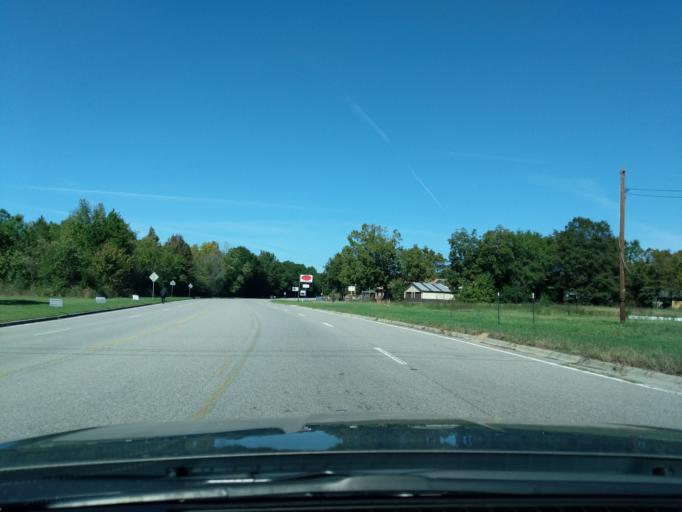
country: US
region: Georgia
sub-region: Richmond County
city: Augusta
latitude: 33.4303
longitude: -82.0065
